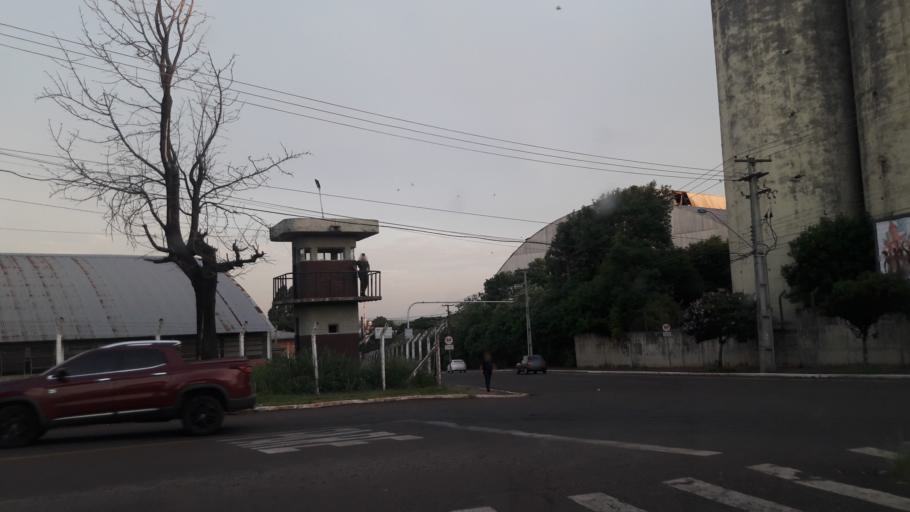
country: BR
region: Parana
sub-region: Cascavel
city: Cascavel
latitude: -24.9650
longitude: -53.4505
